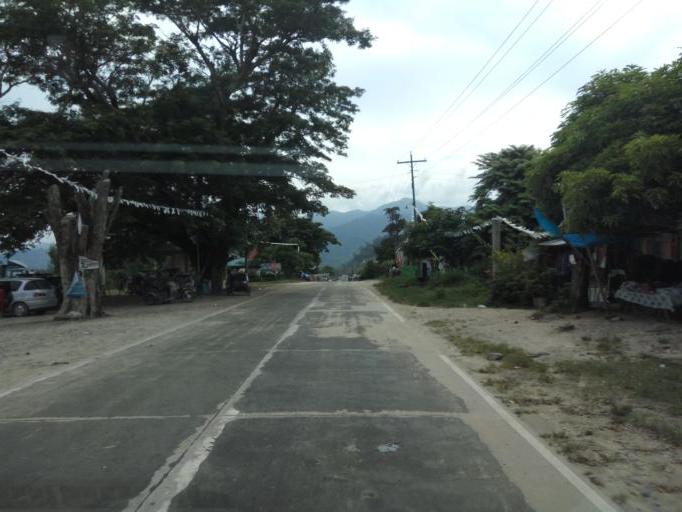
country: PH
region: Central Luzon
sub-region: Province of Aurora
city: Dinalongan
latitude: 16.0774
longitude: 121.7696
